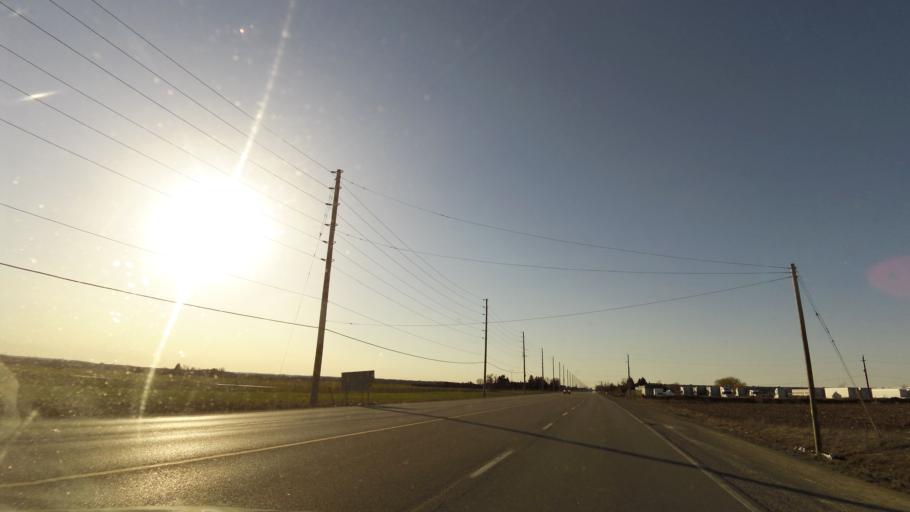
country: CA
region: Ontario
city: Brampton
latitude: 43.8408
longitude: -79.7089
